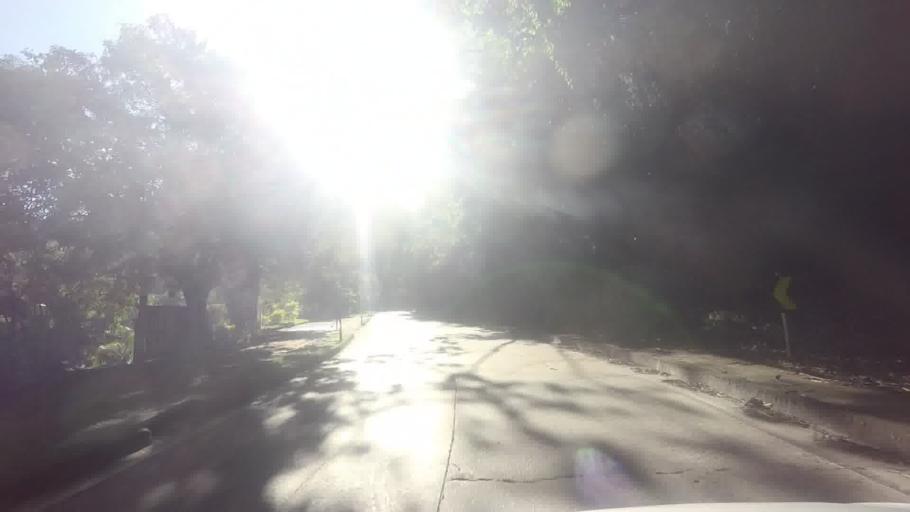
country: BR
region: Rio de Janeiro
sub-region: Petropolis
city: Petropolis
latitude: -22.5866
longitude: -43.2642
